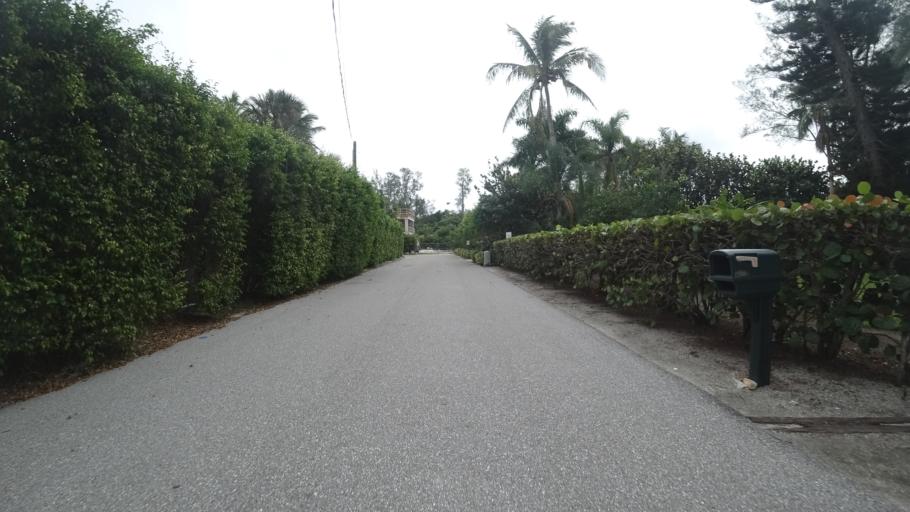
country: US
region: Florida
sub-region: Manatee County
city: Longboat Key
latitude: 27.4257
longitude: -82.6750
